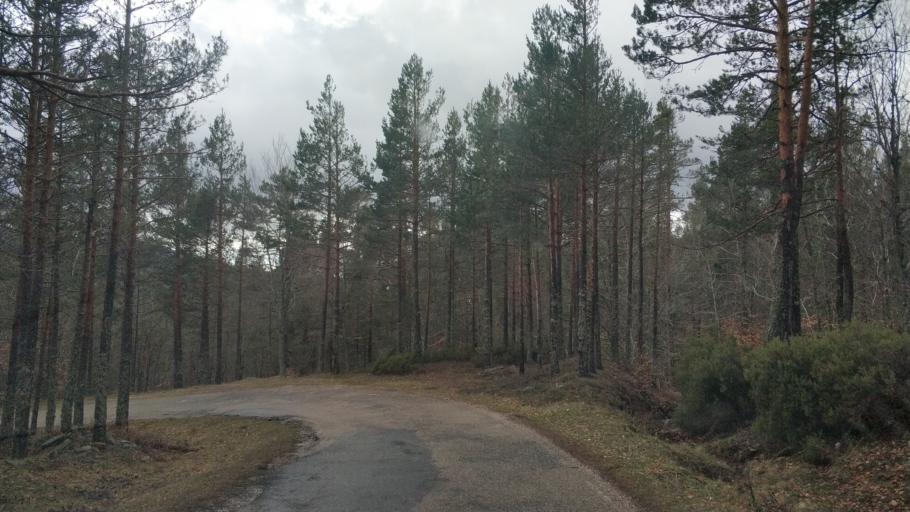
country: ES
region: Castille and Leon
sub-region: Provincia de Burgos
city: Neila
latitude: 42.0445
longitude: -3.0184
